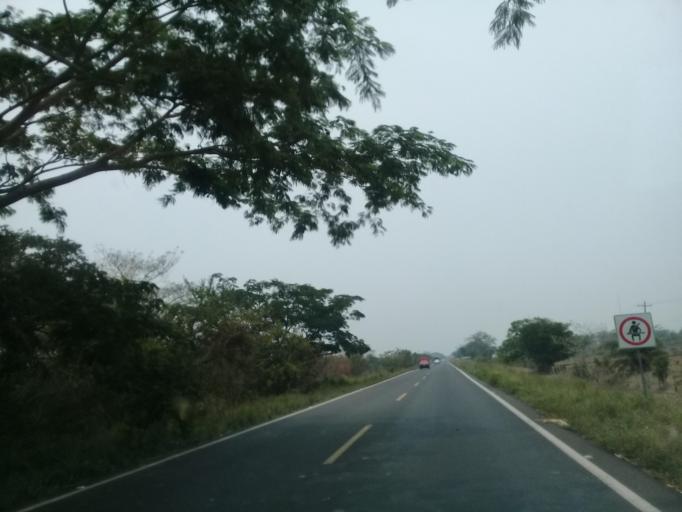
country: MX
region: Veracruz
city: Paso del Toro
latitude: 18.9778
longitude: -96.1764
